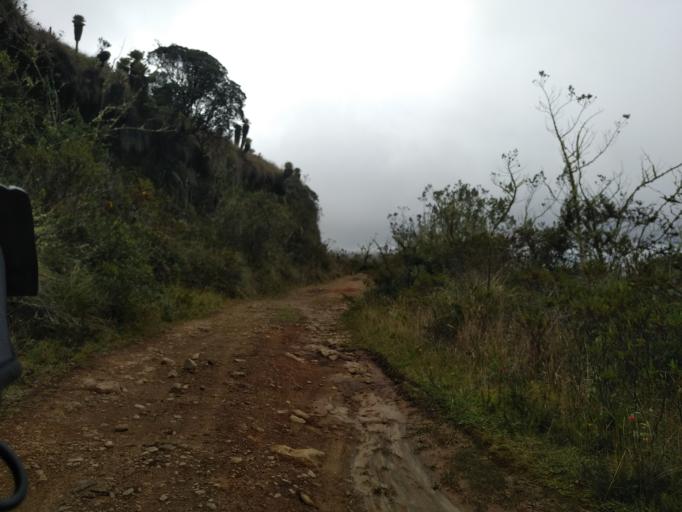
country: EC
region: Carchi
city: San Gabriel
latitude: 0.6944
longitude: -77.8462
